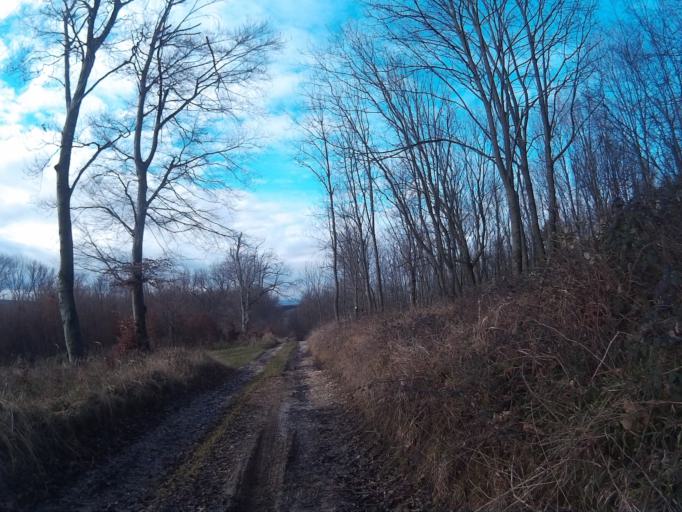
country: HU
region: Veszprem
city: Urkut
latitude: 47.1209
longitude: 17.6743
